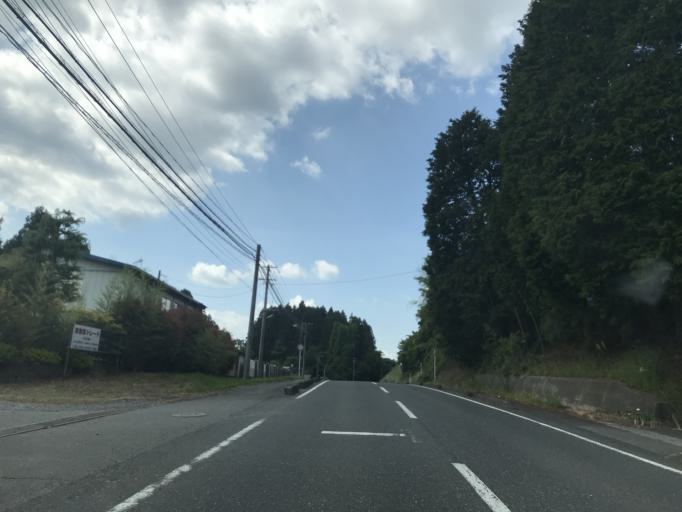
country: JP
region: Miyagi
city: Furukawa
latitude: 38.7507
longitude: 140.9539
